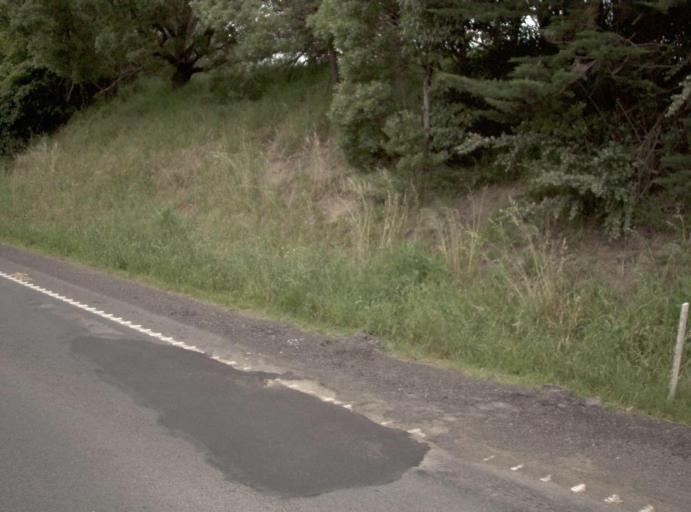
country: AU
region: Victoria
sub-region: Baw Baw
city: Warragul
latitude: -38.4470
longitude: 145.8626
